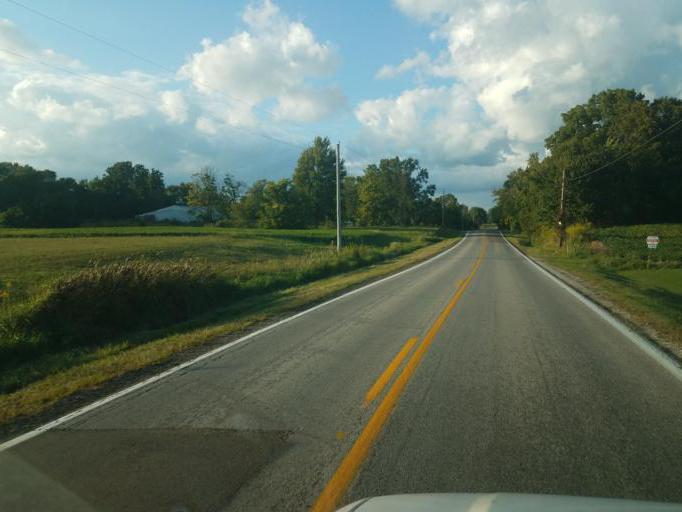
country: US
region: Ohio
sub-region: Knox County
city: Centerburg
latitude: 40.4532
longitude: -82.6970
